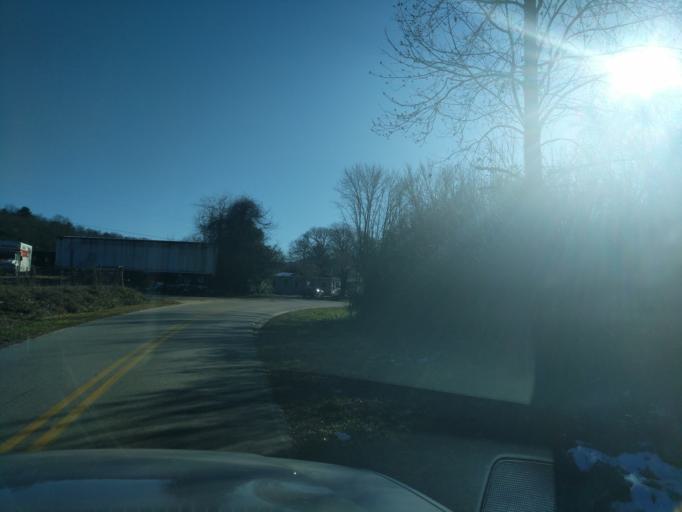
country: US
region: Georgia
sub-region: Towns County
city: Hiawassee
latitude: 34.9406
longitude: -83.7348
